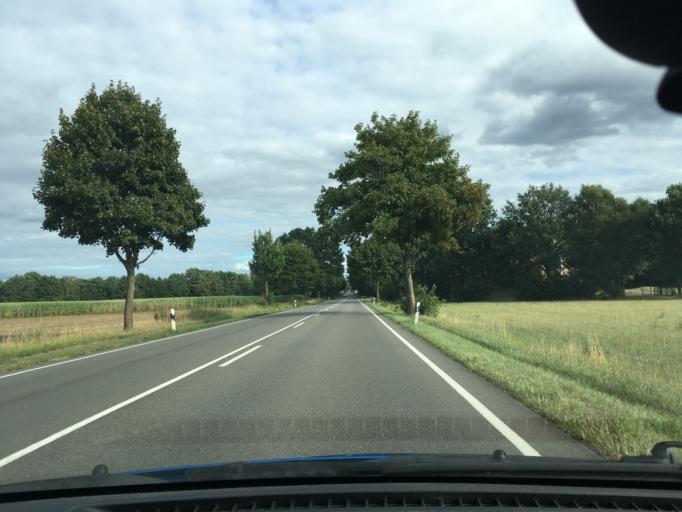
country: DE
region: Lower Saxony
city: Neu Wulmstorf
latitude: 53.4322
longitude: 9.7764
